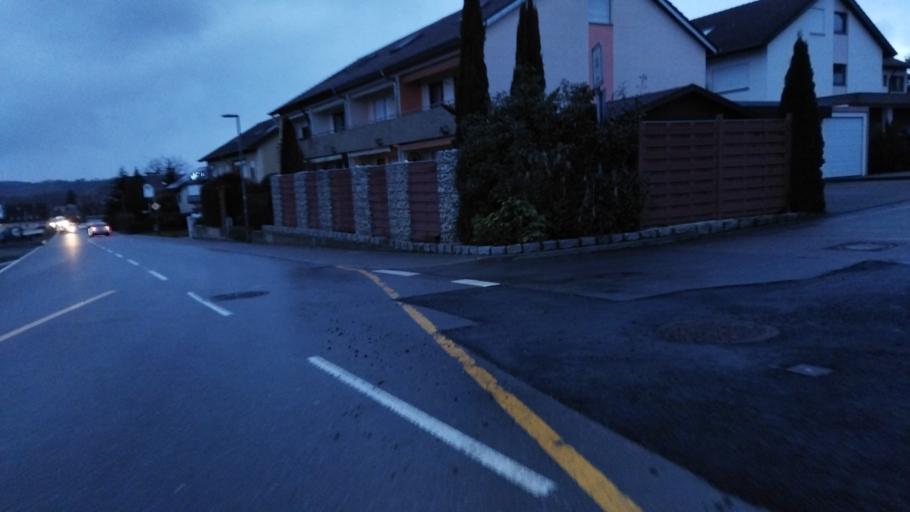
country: DE
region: Baden-Wuerttemberg
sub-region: Regierungsbezirk Stuttgart
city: Untereisesheim
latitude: 49.2174
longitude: 9.2203
